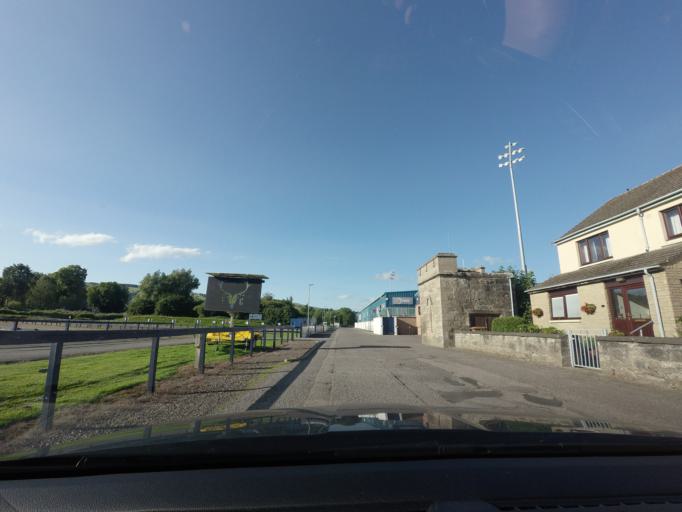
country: GB
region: Scotland
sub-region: Highland
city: Dingwall
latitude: 57.5953
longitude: -4.4204
